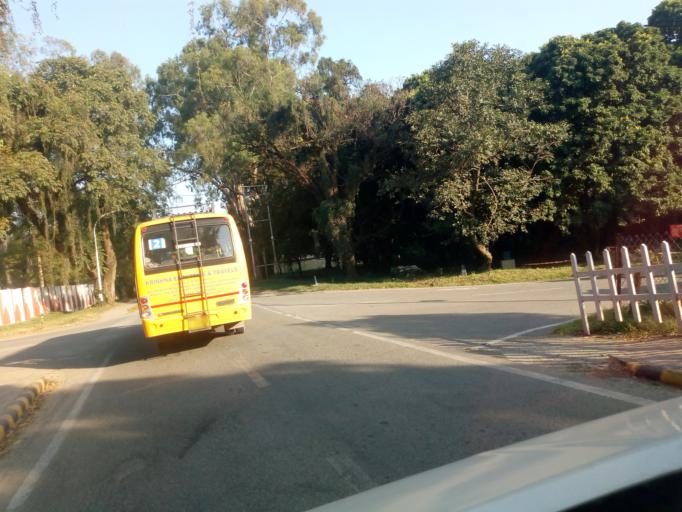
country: IN
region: Uttarakhand
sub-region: Dehradun
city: Dehradun
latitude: 30.3520
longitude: 78.0384
